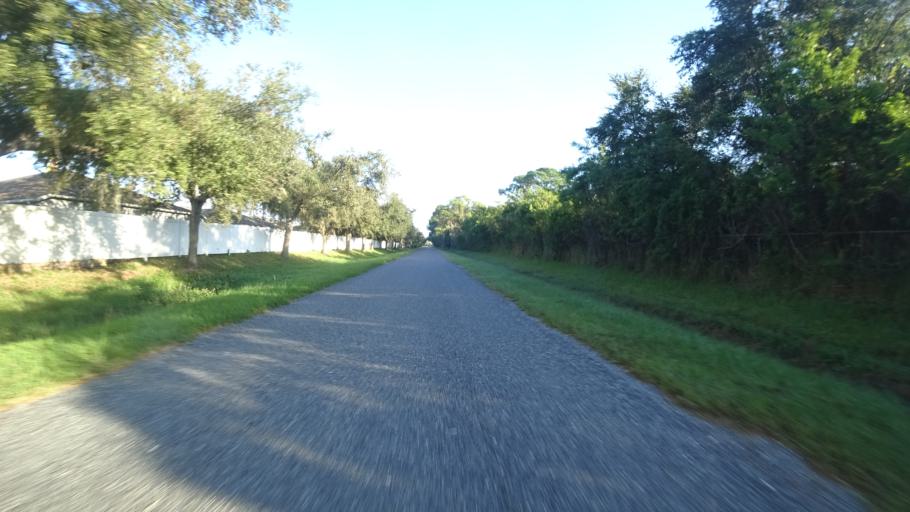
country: US
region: Florida
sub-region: Manatee County
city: Samoset
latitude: 27.4568
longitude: -82.4975
